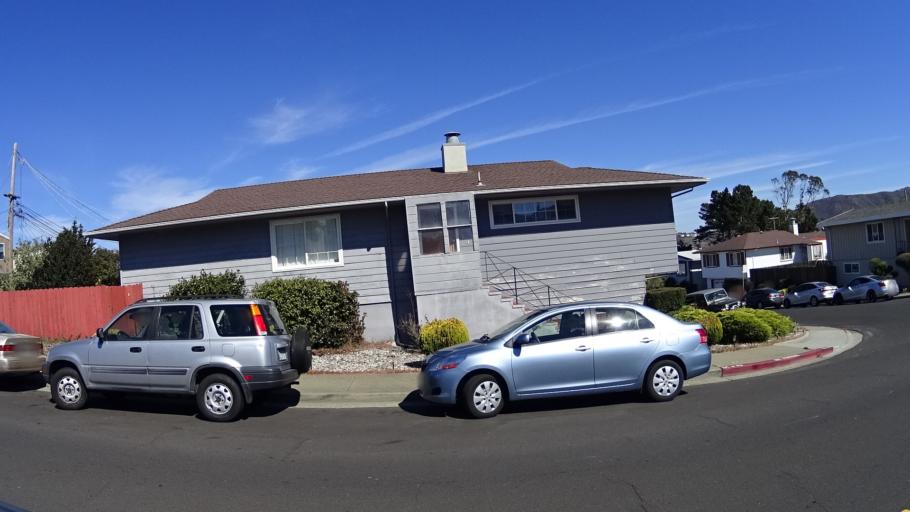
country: US
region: California
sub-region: San Mateo County
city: Broadmoor
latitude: 37.6818
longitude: -122.4763
